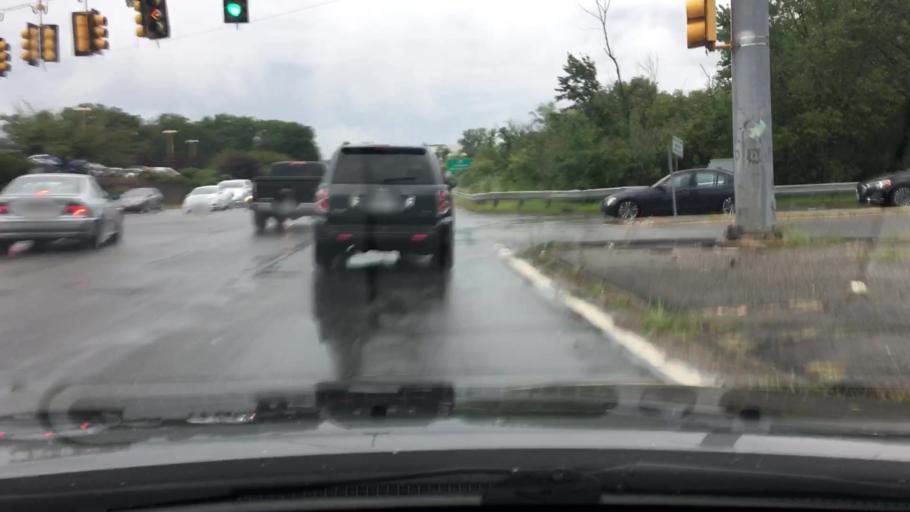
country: US
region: Rhode Island
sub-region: Providence County
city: Valley Falls
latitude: 41.9355
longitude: -71.3508
